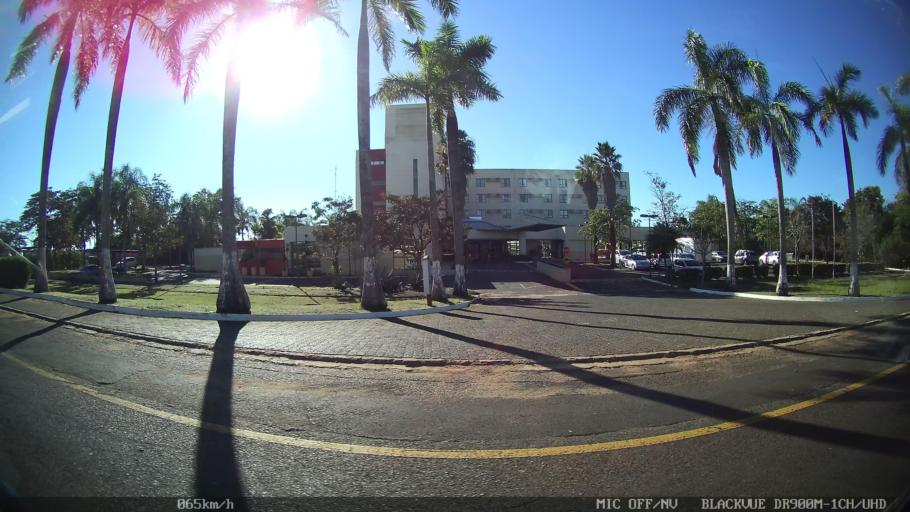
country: BR
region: Sao Paulo
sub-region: Franca
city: Franca
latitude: -20.5654
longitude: -47.3940
